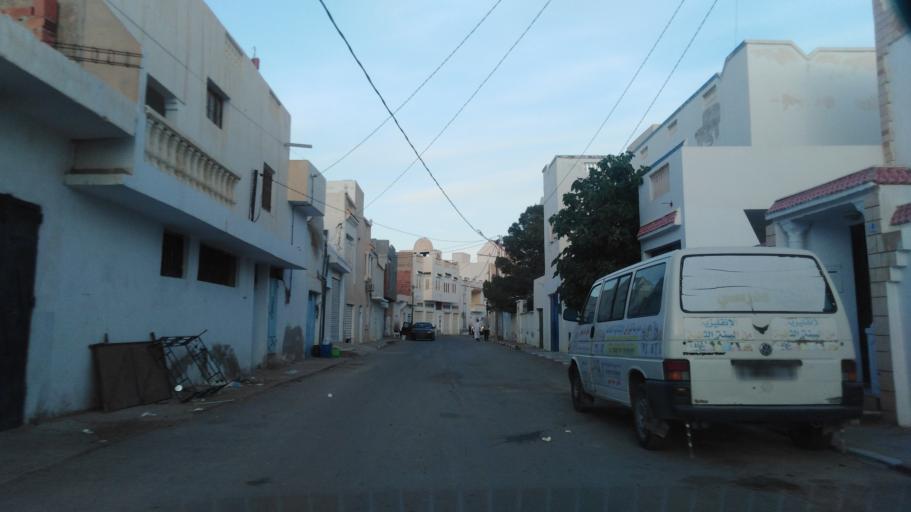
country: TN
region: Tataouine
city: Tataouine
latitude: 32.9384
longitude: 10.4526
